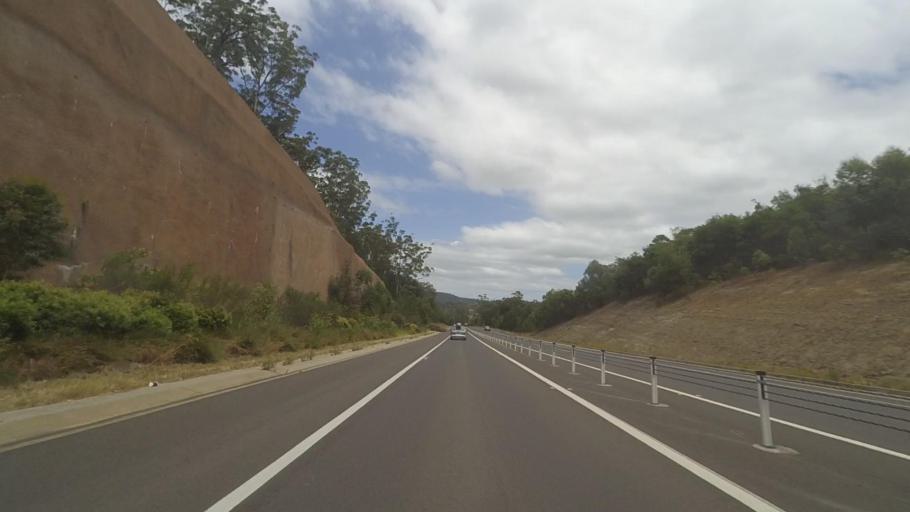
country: AU
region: New South Wales
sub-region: Shoalhaven Shire
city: Milton
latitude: -35.2081
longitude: 150.4387
